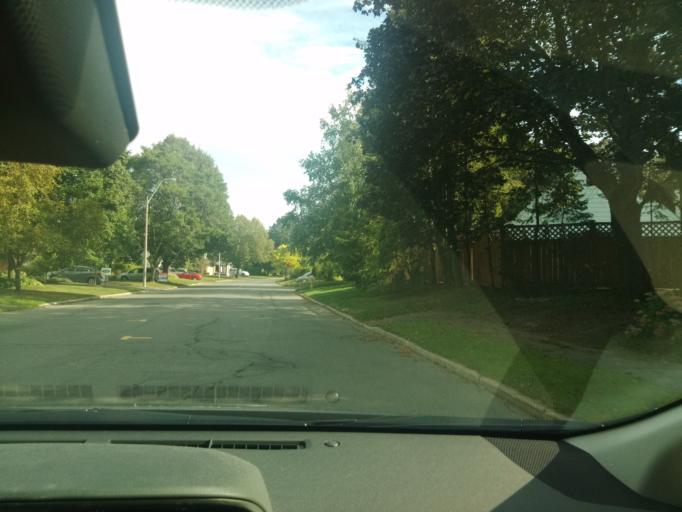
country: CA
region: Ontario
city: Ottawa
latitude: 45.3921
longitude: -75.6415
